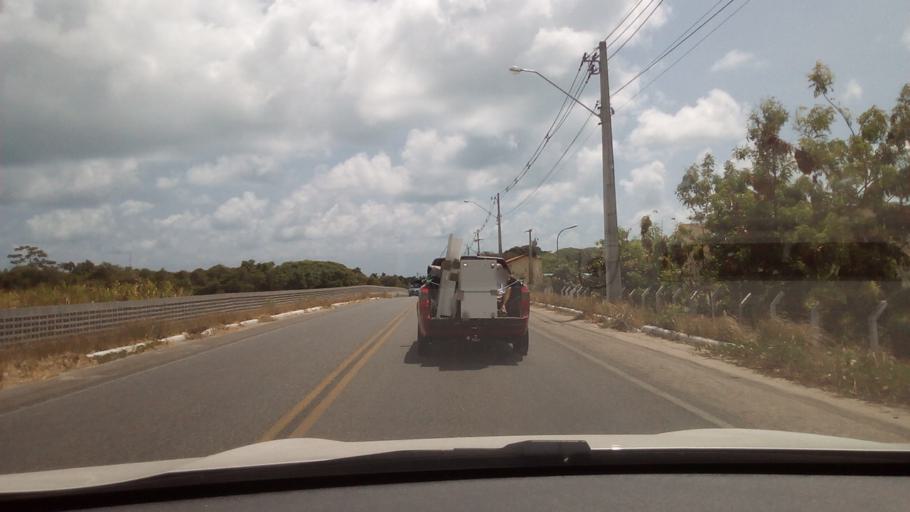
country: BR
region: Paraiba
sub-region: Joao Pessoa
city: Joao Pessoa
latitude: -7.1985
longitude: -34.8149
